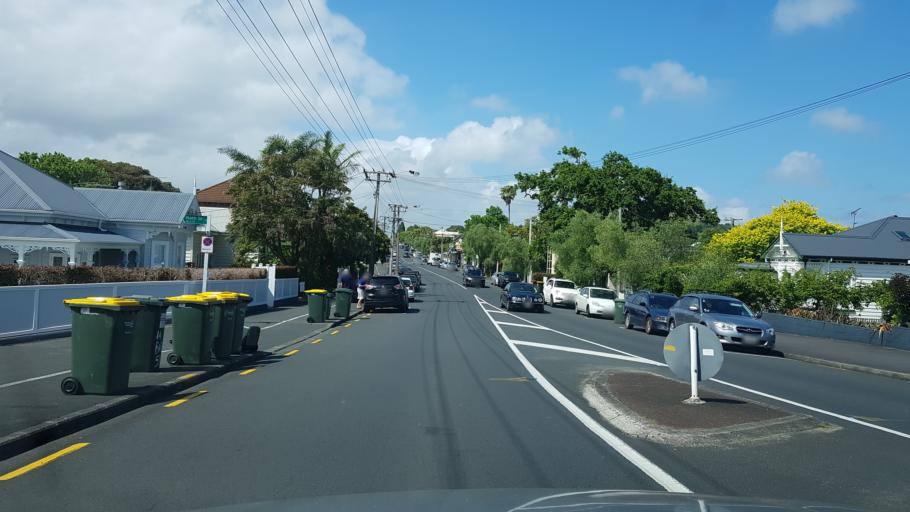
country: NZ
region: Auckland
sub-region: Auckland
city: North Shore
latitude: -36.8197
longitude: 174.8056
